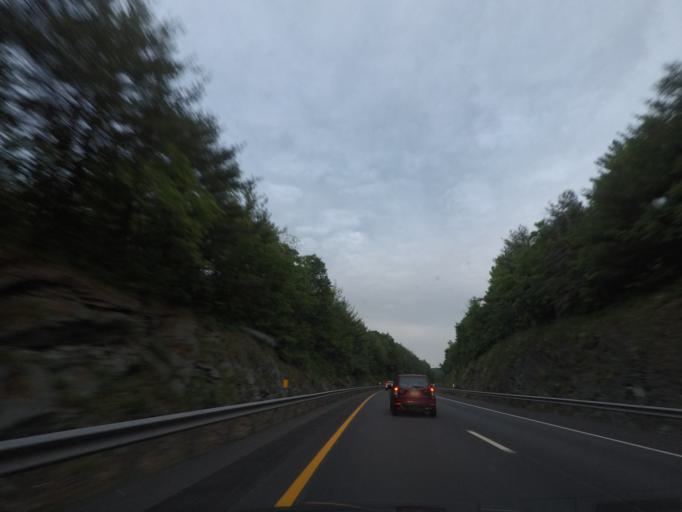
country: US
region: New York
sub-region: Rensselaer County
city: Nassau
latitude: 42.4483
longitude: -73.5708
